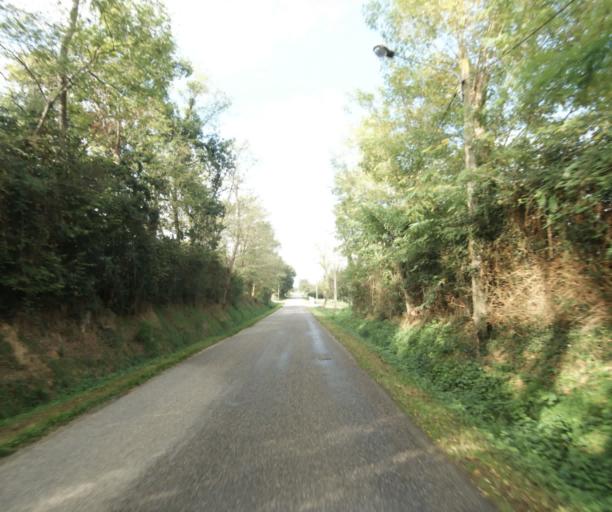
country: FR
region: Midi-Pyrenees
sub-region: Departement du Gers
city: Eauze
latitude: 43.8666
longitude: 0.1011
